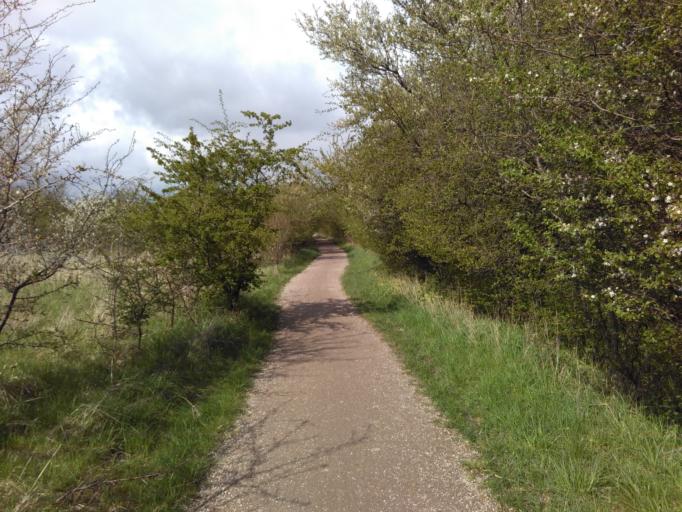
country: DK
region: Capital Region
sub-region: Tarnby Kommune
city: Tarnby
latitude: 55.6446
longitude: 12.5776
